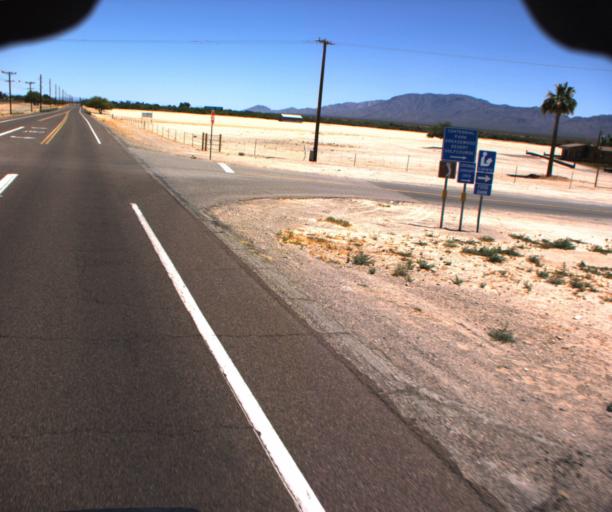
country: US
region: Arizona
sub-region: La Paz County
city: Salome
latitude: 33.8128
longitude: -113.5585
